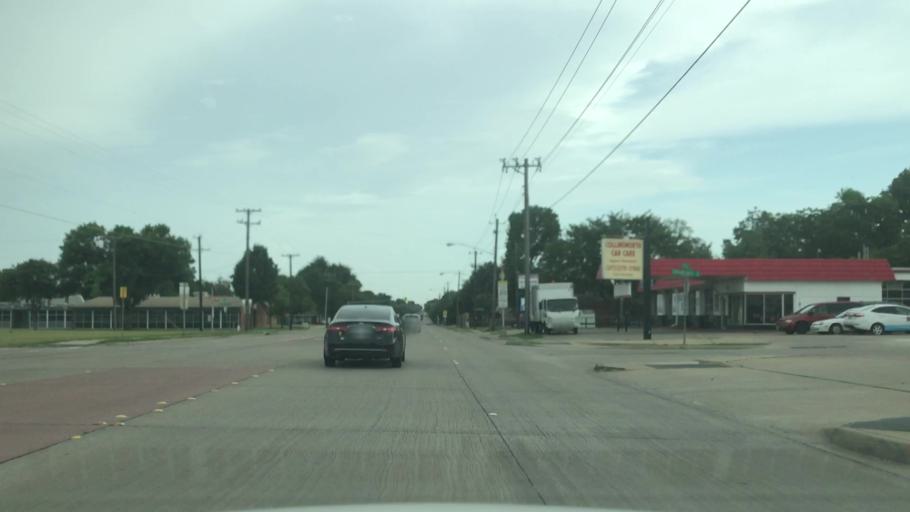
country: US
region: Texas
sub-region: Dallas County
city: Garland
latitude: 32.8774
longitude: -96.6483
